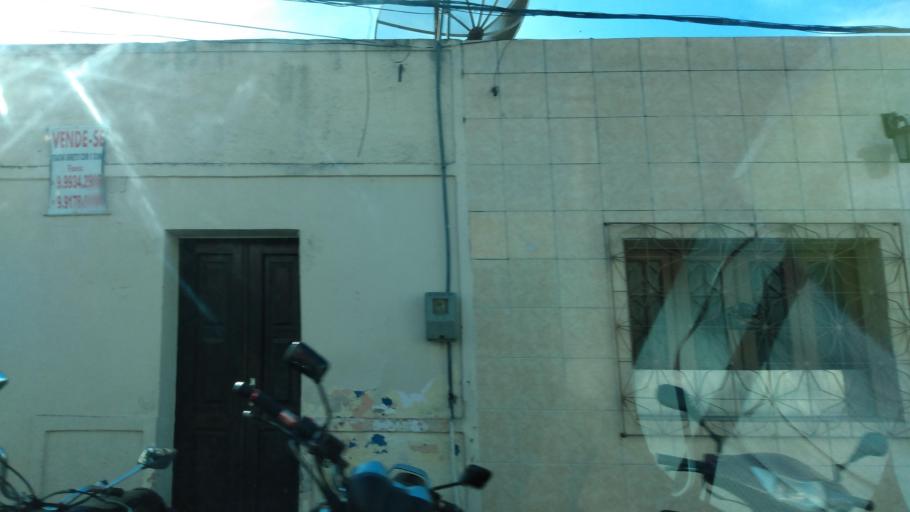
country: ET
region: Oromiya
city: Gore
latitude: 8.2011
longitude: 35.5700
